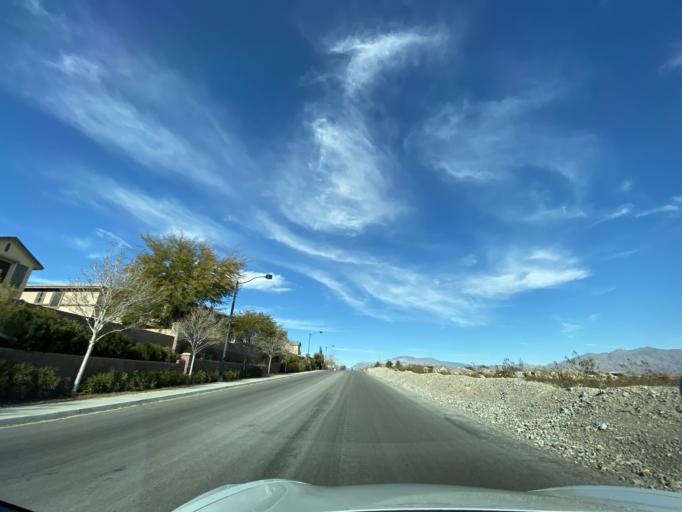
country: US
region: Nevada
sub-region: Clark County
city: Summerlin South
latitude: 36.2868
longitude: -115.3195
